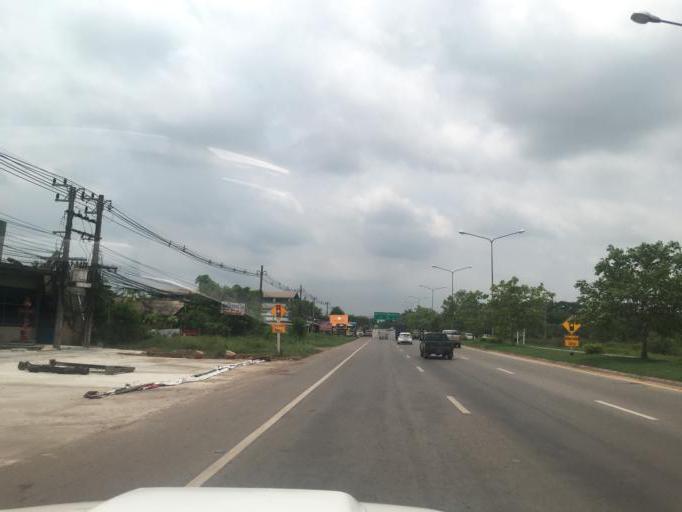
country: TH
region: Changwat Udon Thani
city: Udon Thani
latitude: 17.3927
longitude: 102.7661
